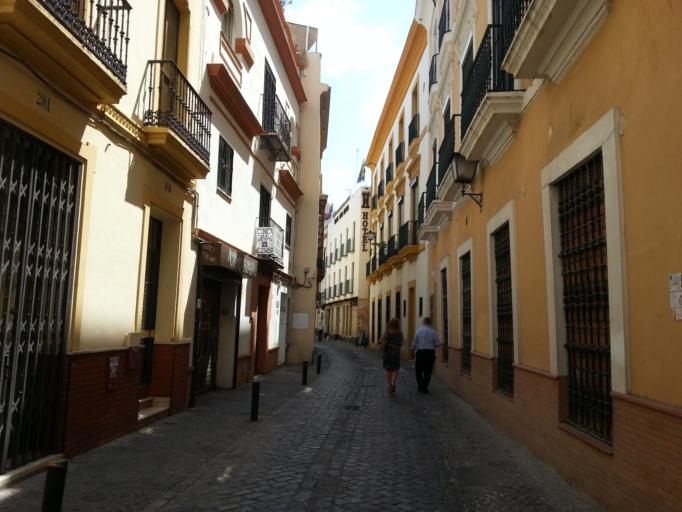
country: ES
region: Andalusia
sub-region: Provincia de Sevilla
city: Sevilla
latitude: 37.3917
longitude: -6.0009
